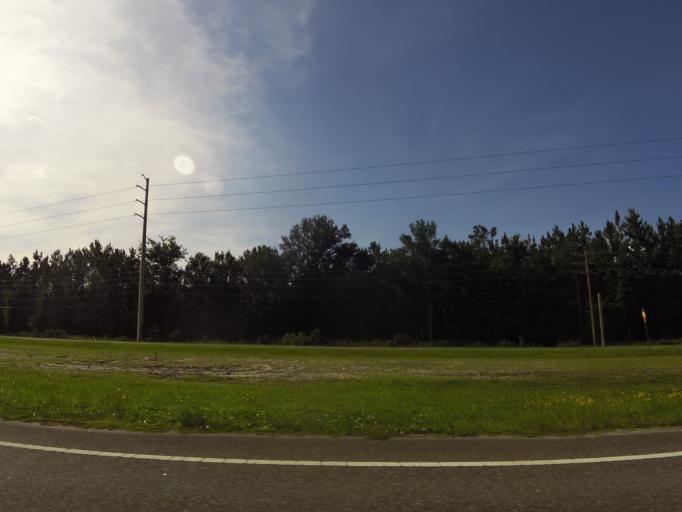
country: US
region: Florida
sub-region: Clay County
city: Green Cove Springs
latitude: 30.0138
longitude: -81.6016
